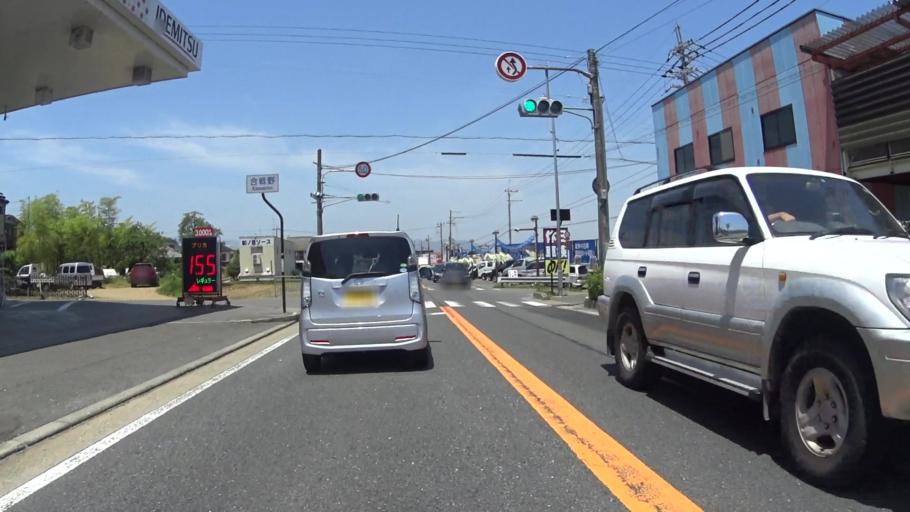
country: JP
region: Kyoto
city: Kameoka
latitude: 34.9998
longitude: 135.6099
